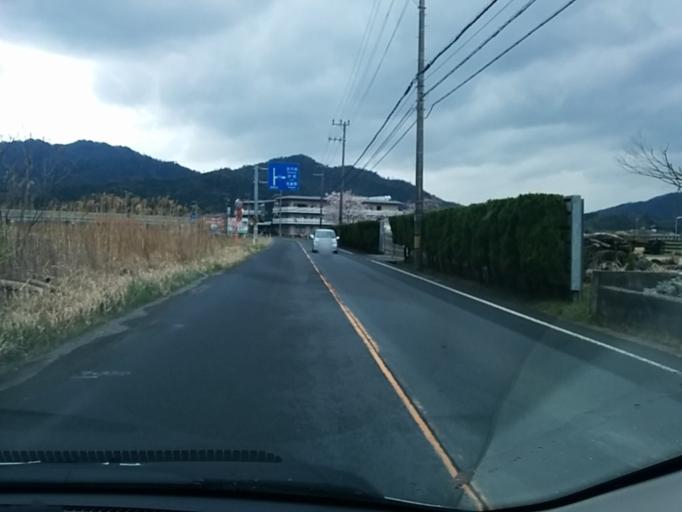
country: JP
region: Kyoto
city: Miyazu
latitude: 35.5544
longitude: 135.1611
